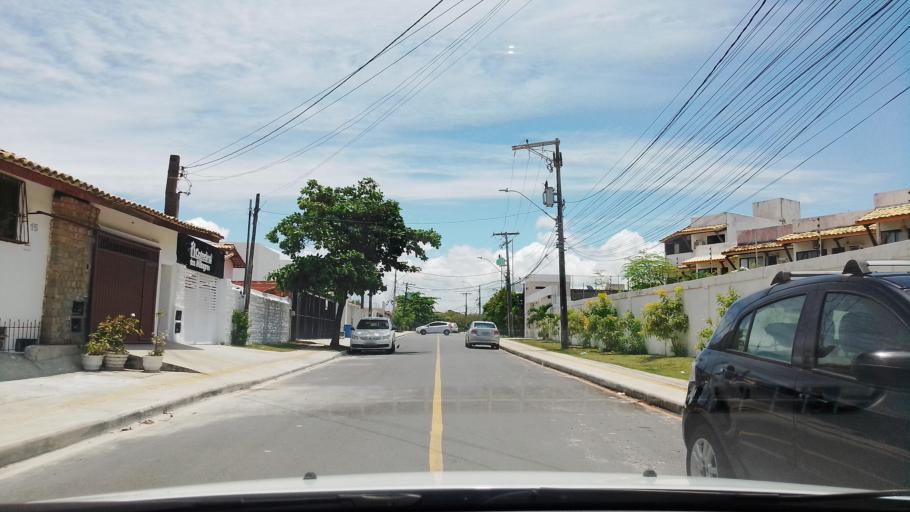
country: BR
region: Bahia
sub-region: Lauro De Freitas
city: Lauro de Freitas
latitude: -12.9339
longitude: -38.3281
